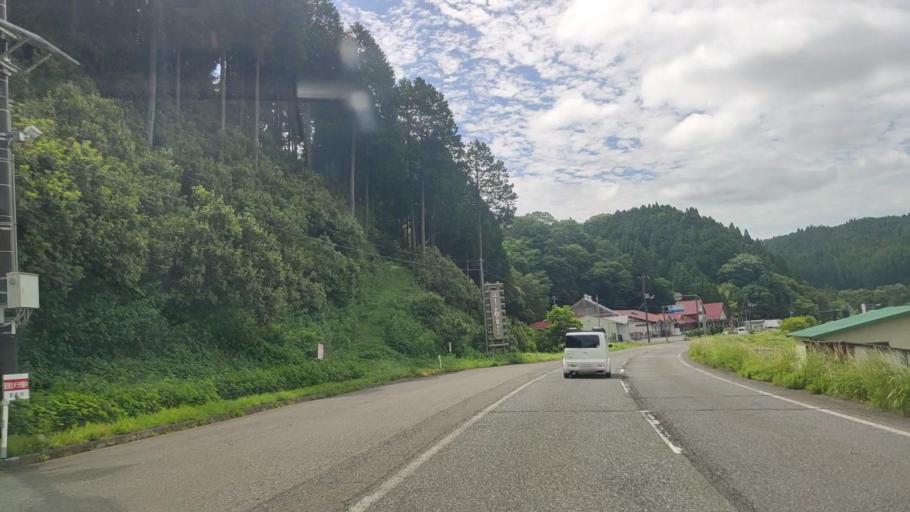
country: JP
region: Okayama
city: Niimi
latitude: 35.1773
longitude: 133.5711
